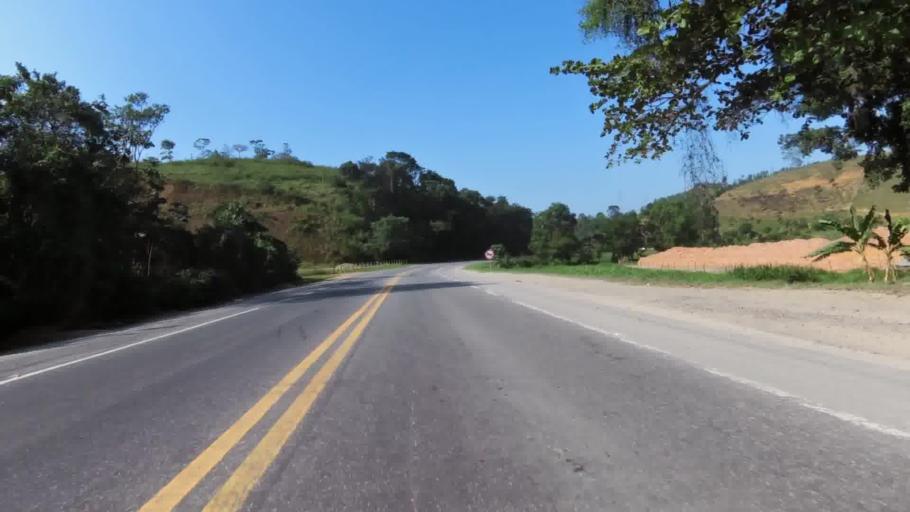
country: BR
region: Espirito Santo
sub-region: Iconha
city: Iconha
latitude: -20.8232
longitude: -40.8515
